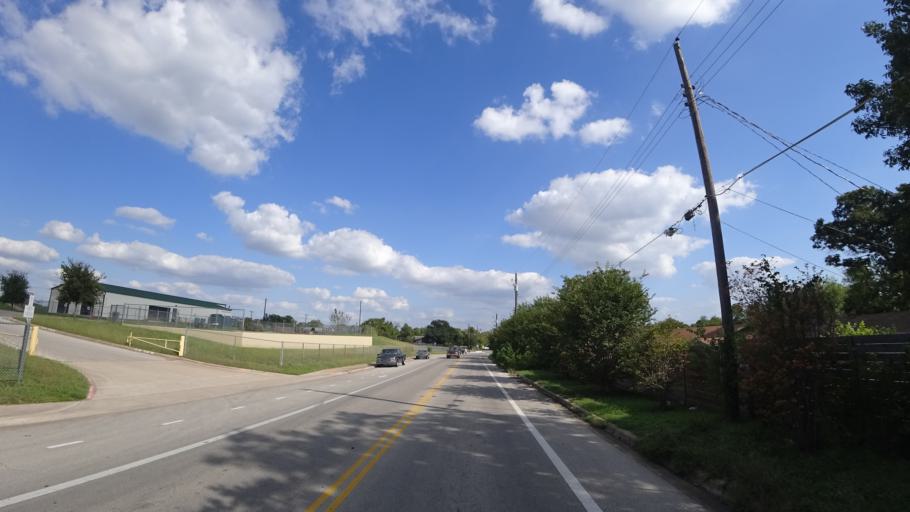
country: US
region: Texas
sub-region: Travis County
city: Wells Branch
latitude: 30.3582
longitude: -97.7071
